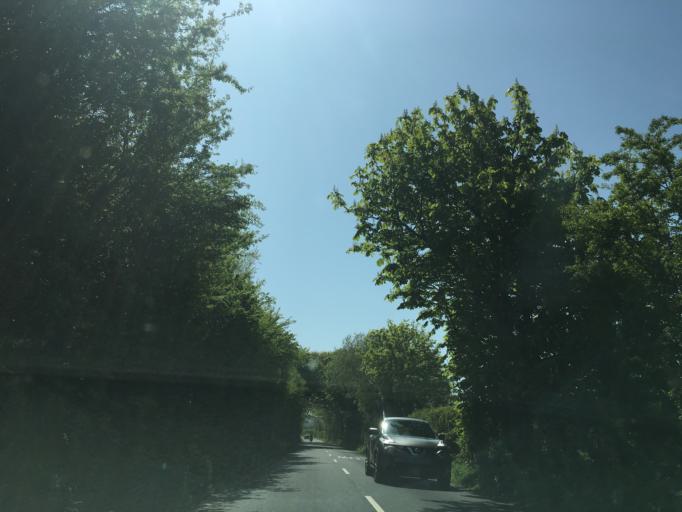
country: GB
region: England
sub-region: Isle of Wight
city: Niton
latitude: 50.5962
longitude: -1.2730
